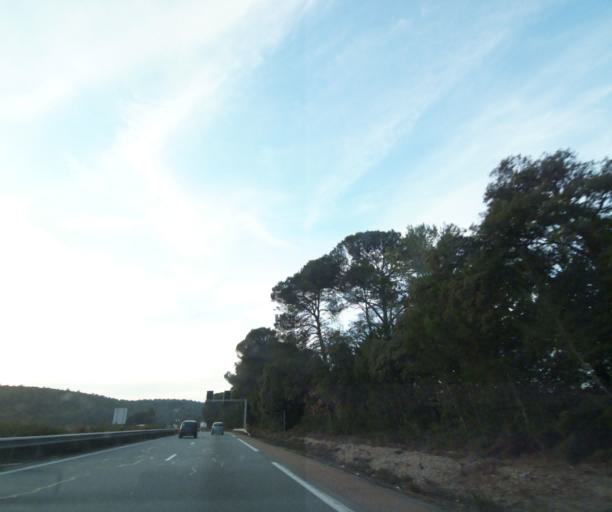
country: FR
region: Provence-Alpes-Cote d'Azur
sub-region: Departement du Var
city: La Motte
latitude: 43.4801
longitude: 6.5190
